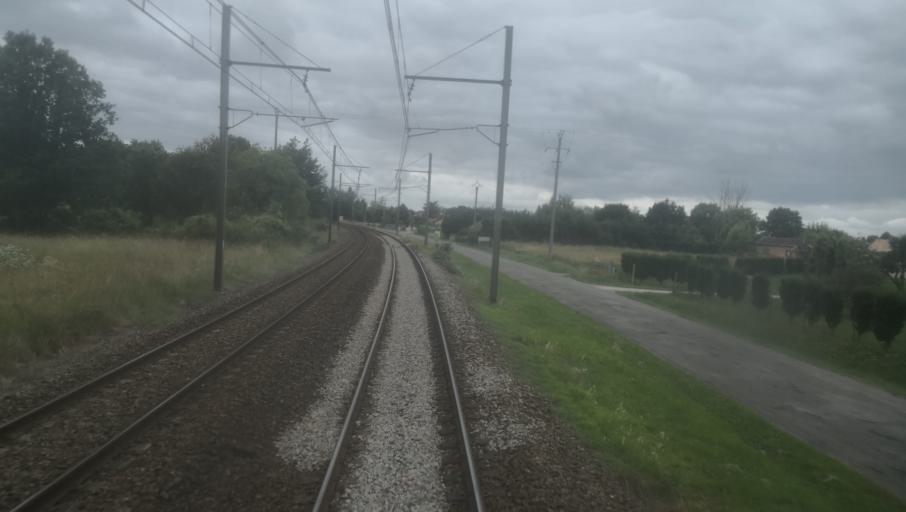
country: FR
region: Midi-Pyrenees
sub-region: Departement du Tarn-et-Garonne
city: Saint-Porquier
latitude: 44.0349
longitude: 1.2220
